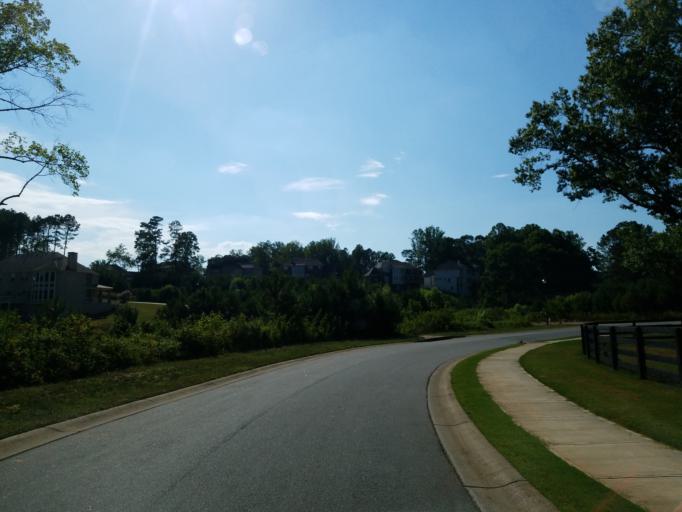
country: US
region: Georgia
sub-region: Fulton County
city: Milton
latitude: 34.1837
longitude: -84.3244
